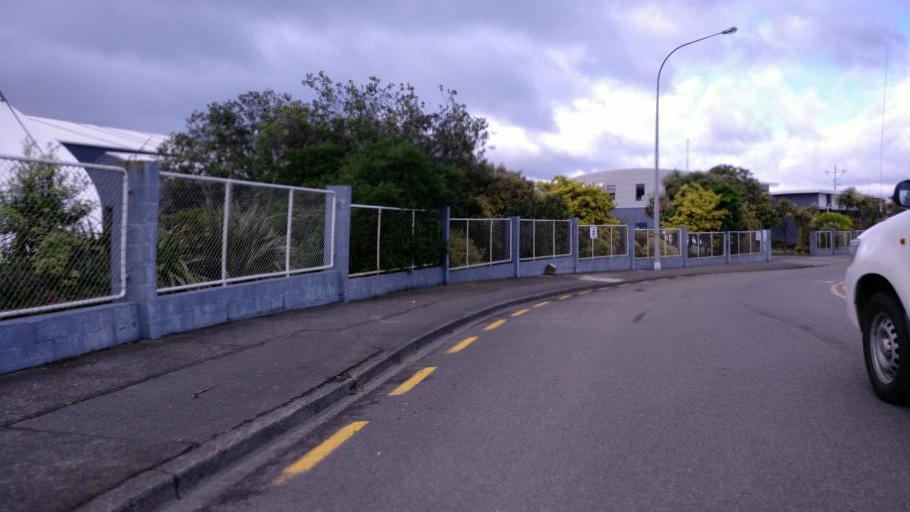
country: NZ
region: Wellington
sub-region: Lower Hutt City
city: Lower Hutt
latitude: -41.2371
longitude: 174.9098
